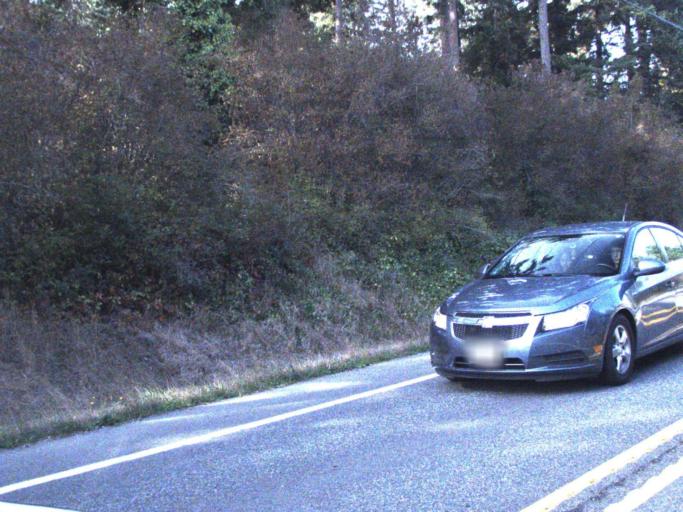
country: US
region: Washington
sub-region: Island County
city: Coupeville
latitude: 48.2462
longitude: -122.7141
